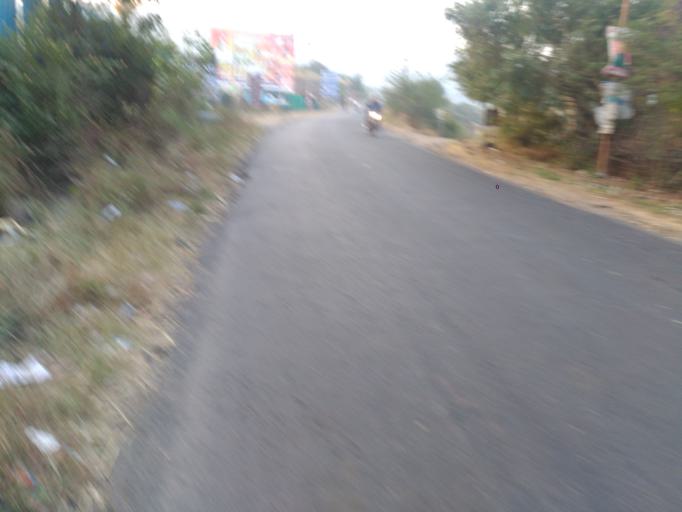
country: IN
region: Maharashtra
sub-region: Pune Division
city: Khed
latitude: 18.4252
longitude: 73.9018
